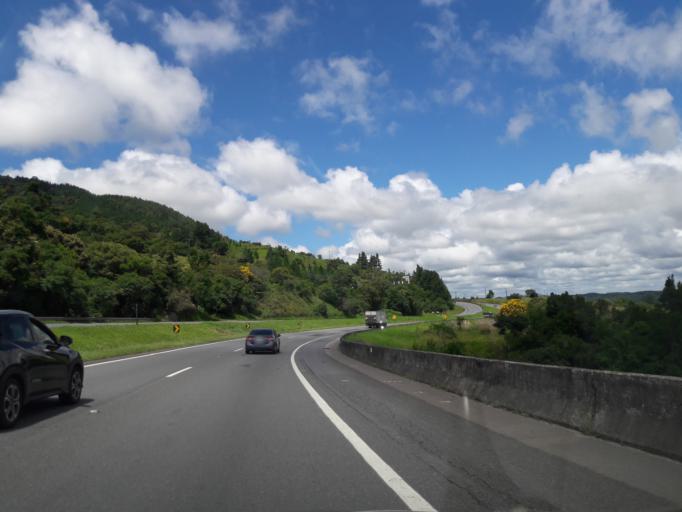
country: BR
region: Parana
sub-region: Campina Grande Do Sul
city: Campina Grande do Sul
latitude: -25.1506
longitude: -48.8594
